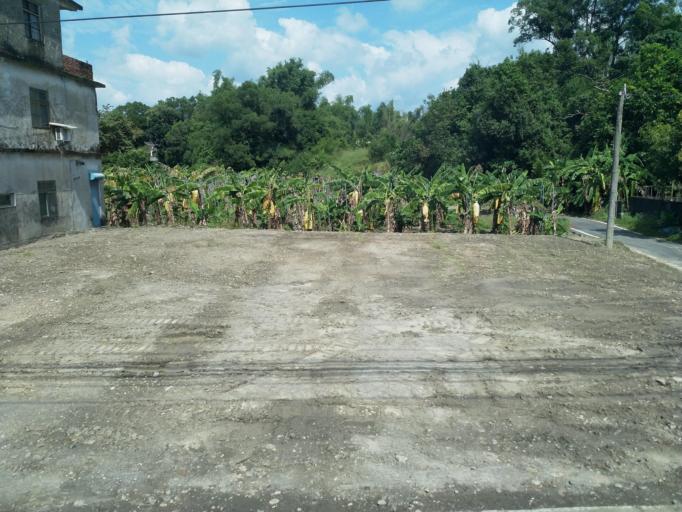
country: TW
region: Taiwan
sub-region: Pingtung
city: Pingtung
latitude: 22.8823
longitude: 120.5580
